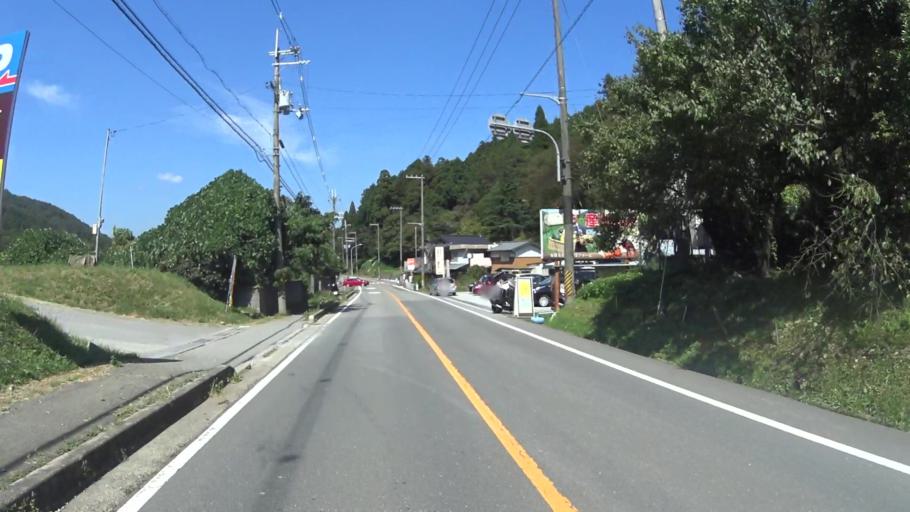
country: JP
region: Kyoto
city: Kameoka
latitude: 34.9426
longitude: 135.4966
